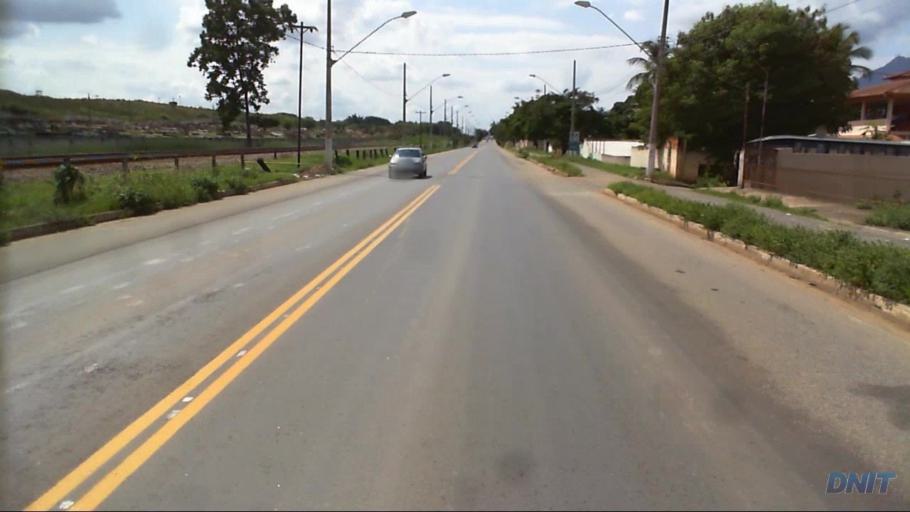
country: BR
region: Minas Gerais
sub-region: Governador Valadares
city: Governador Valadares
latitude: -18.9105
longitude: -41.9953
